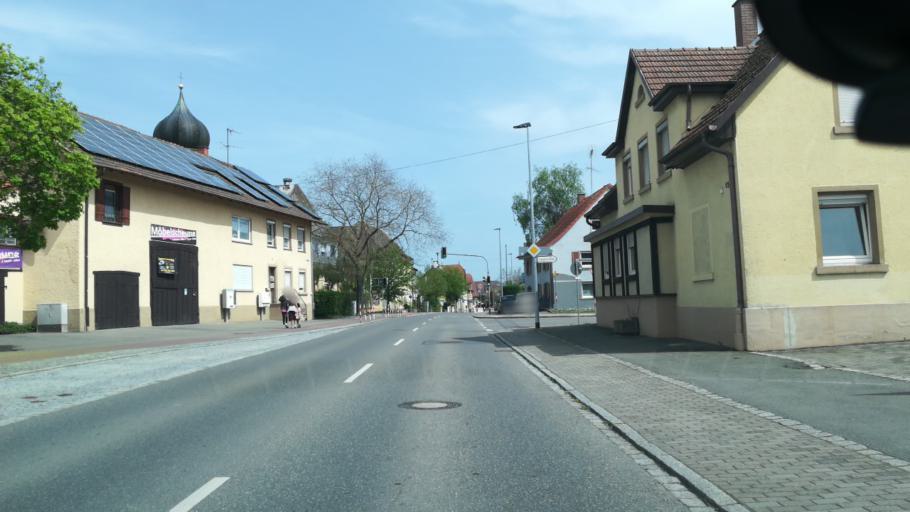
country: DE
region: Baden-Wuerttemberg
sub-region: Freiburg Region
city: Moos
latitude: 47.7527
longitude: 8.9316
